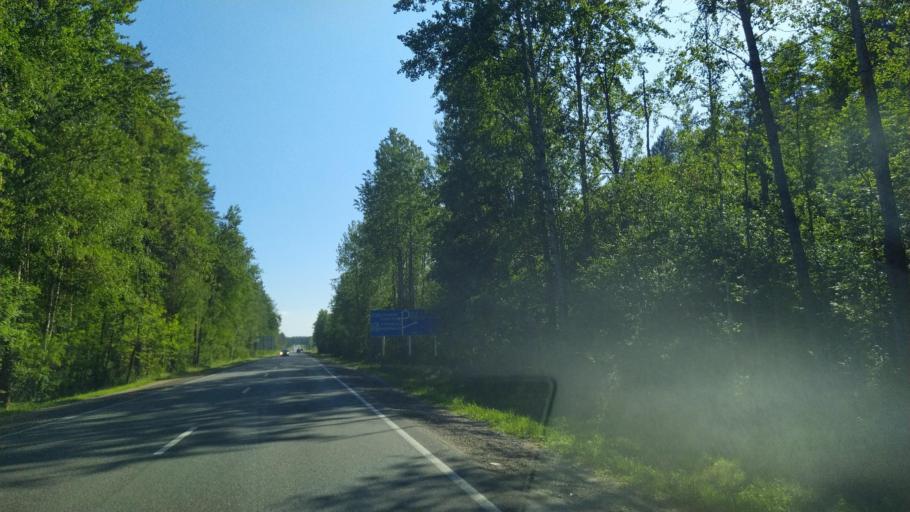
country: RU
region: Leningrad
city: Kirovsk
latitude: 59.9189
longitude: 30.9414
